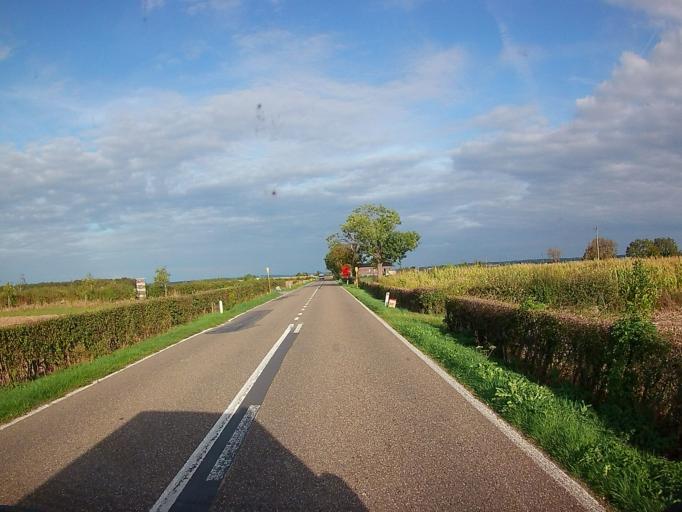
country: BE
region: Wallonia
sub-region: Province de Liege
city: Aubel
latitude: 50.7168
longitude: 5.8522
